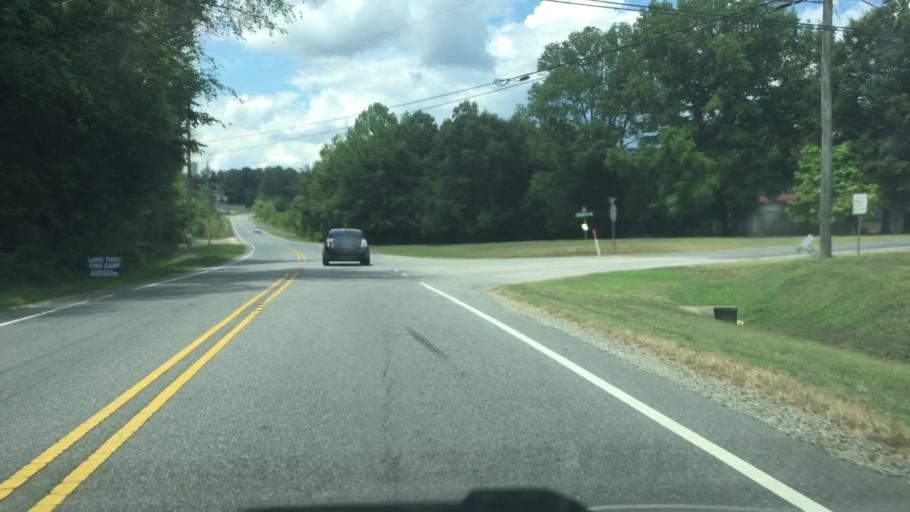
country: US
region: North Carolina
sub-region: Rowan County
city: Enochville
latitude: 35.4826
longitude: -80.7117
